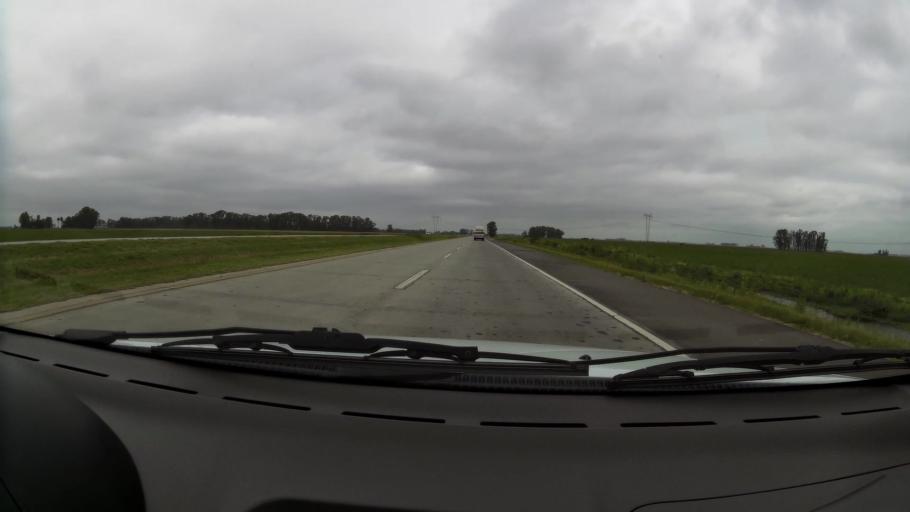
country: AR
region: Buenos Aires
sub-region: Partido de Brandsen
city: Brandsen
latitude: -35.0232
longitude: -58.2492
